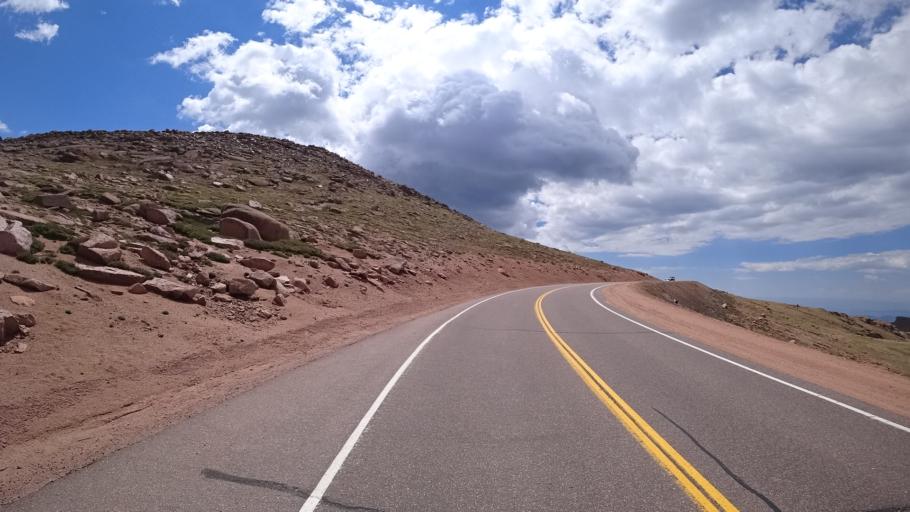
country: US
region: Colorado
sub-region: El Paso County
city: Cascade-Chipita Park
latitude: 38.8512
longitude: -105.0615
